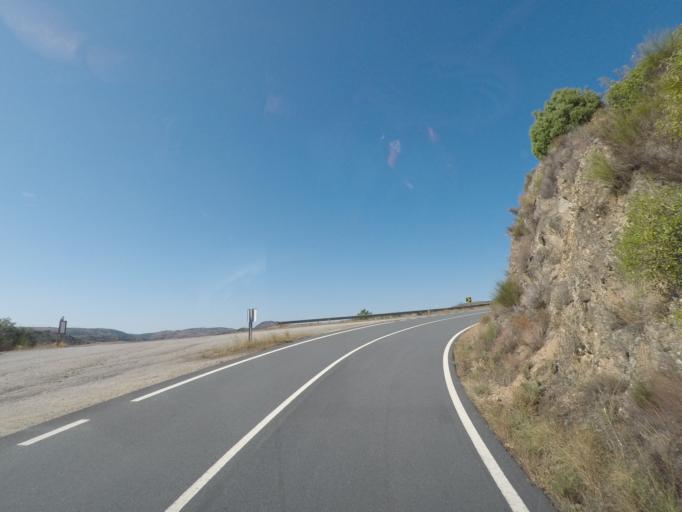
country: ES
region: Castille and Leon
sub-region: Provincia de Salamanca
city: Villarino de los Aires
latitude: 41.2985
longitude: -6.4811
